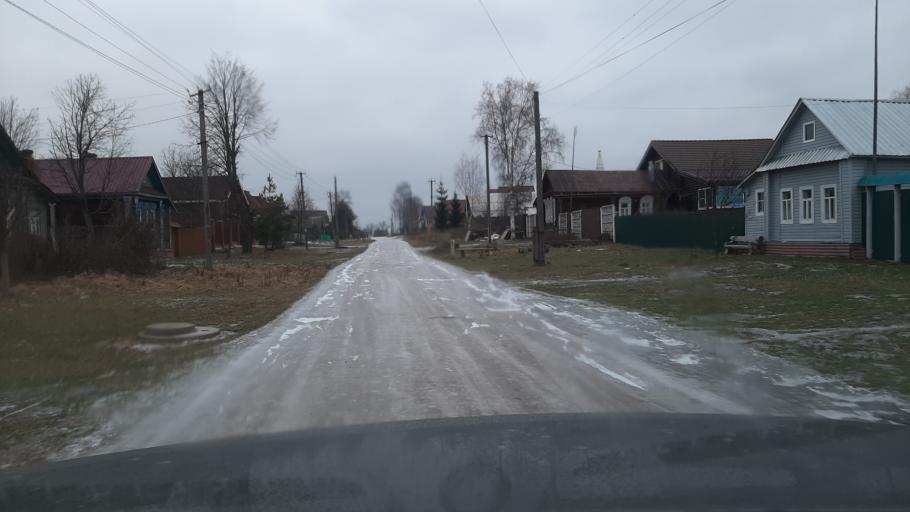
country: RU
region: Ivanovo
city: Shuya
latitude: 56.9929
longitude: 41.4065
